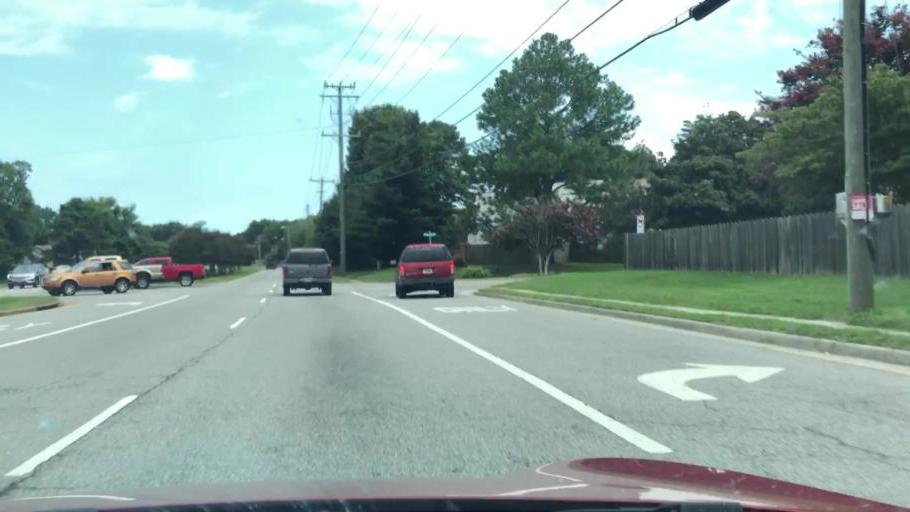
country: US
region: Virginia
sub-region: City of Chesapeake
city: Chesapeake
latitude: 36.8792
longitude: -76.1331
